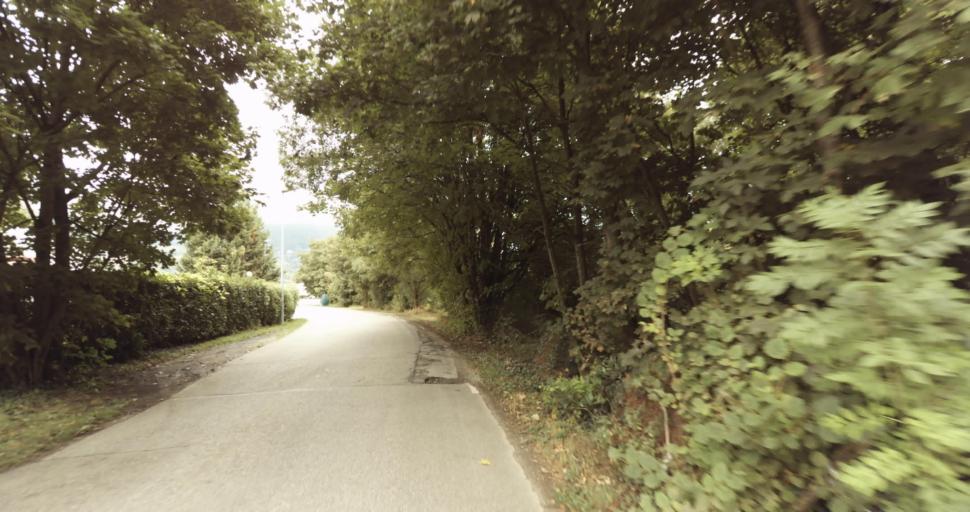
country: FR
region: Rhone-Alpes
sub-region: Departement de la Savoie
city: La Ravoire
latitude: 45.5669
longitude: 5.9631
